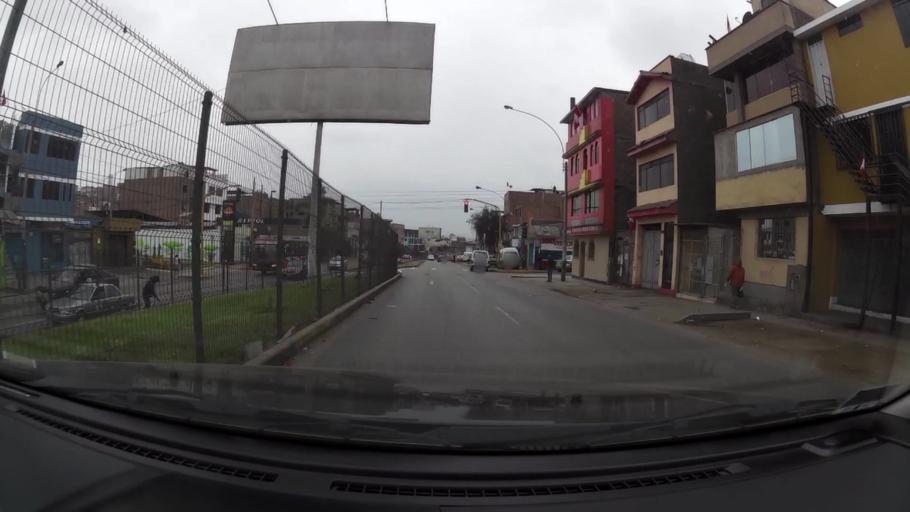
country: PE
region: Lima
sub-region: Lima
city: Surco
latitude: -12.1420
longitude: -76.9745
